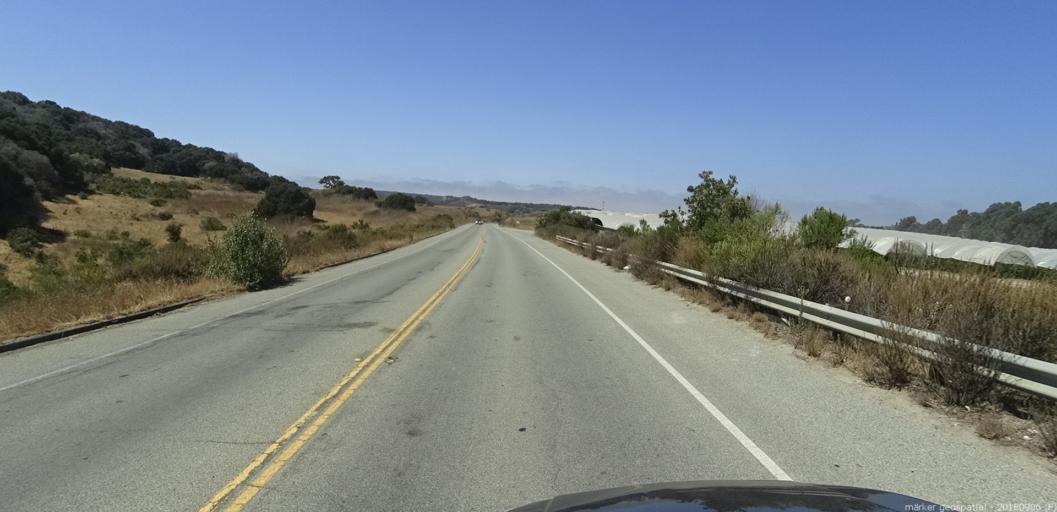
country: US
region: California
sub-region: Monterey County
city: Salinas
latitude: 36.6317
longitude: -121.6939
